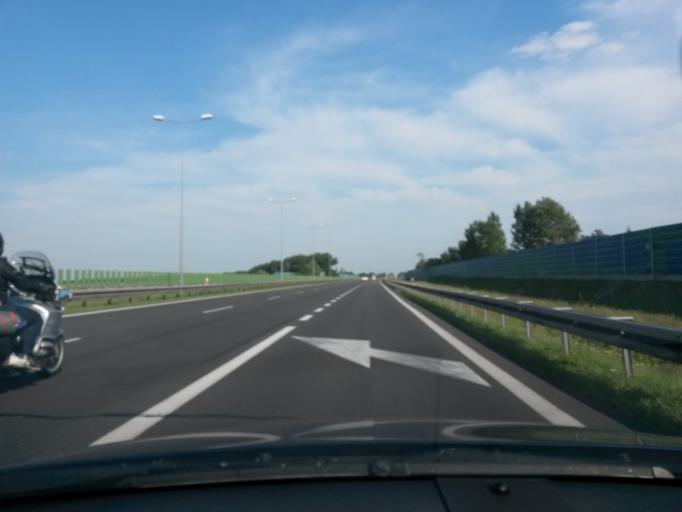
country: PL
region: Greater Poland Voivodeship
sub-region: Powiat wrzesinski
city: Kolaczkowo
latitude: 52.2936
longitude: 17.6557
